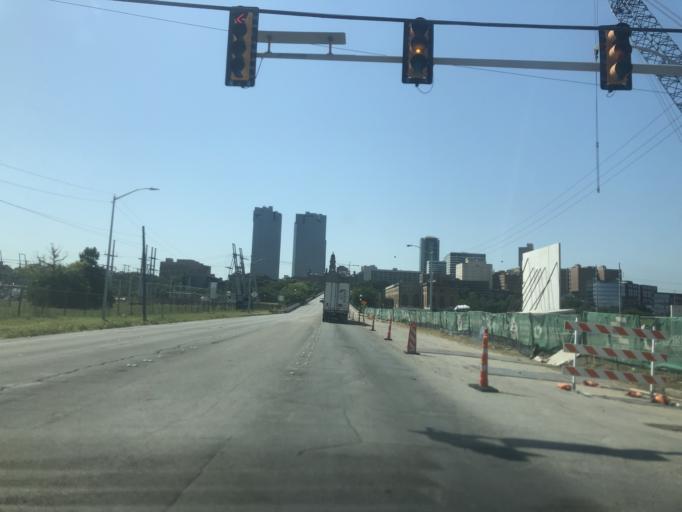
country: US
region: Texas
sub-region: Tarrant County
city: Fort Worth
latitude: 32.7638
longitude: -97.3375
